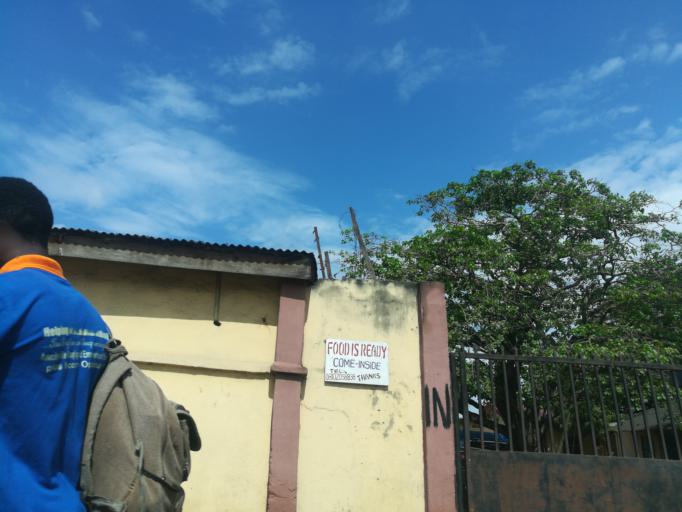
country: NG
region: Lagos
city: Agege
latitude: 6.6253
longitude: 3.3248
